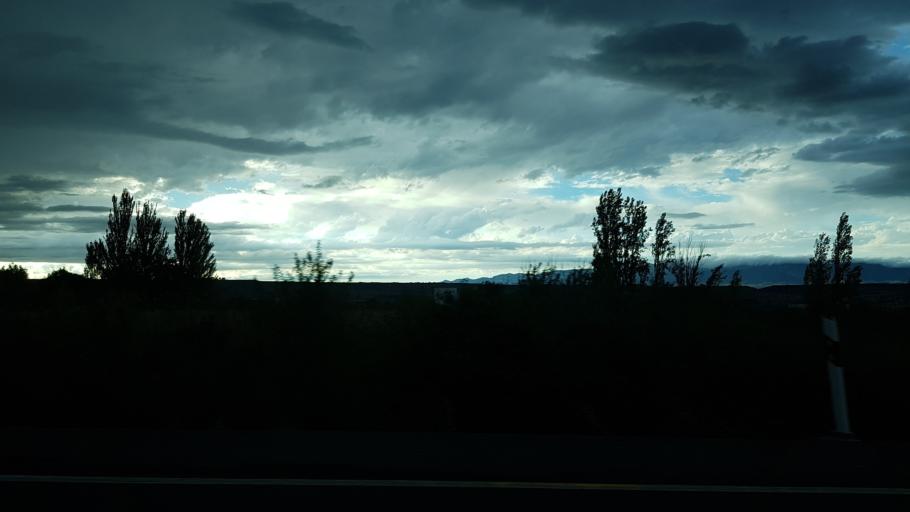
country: ES
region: La Rioja
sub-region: Provincia de La Rioja
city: Lardero
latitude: 42.4369
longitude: -2.4651
